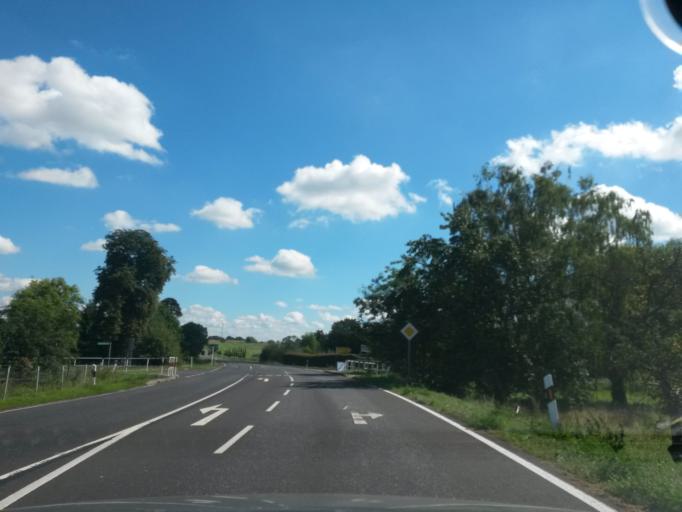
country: DE
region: Brandenburg
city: Schoneberg
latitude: 53.0314
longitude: 14.1145
